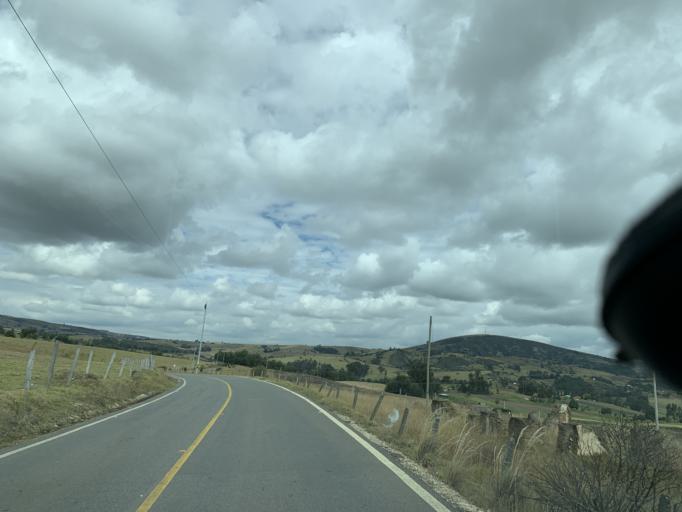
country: CO
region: Boyaca
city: Toca
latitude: 5.5694
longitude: -73.2065
